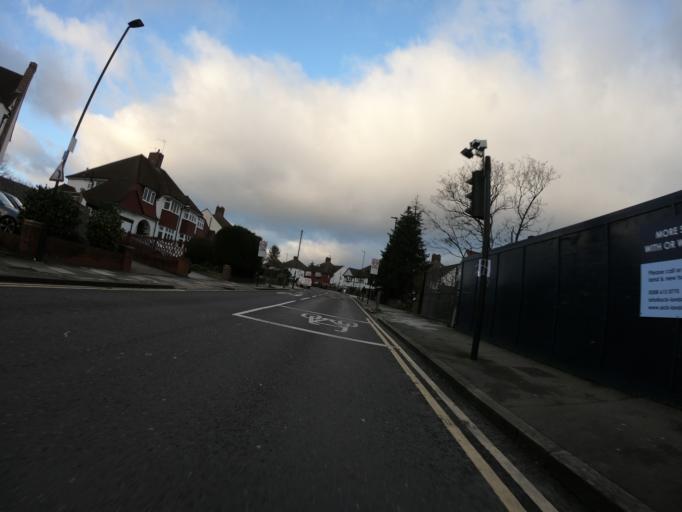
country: GB
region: England
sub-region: Greater London
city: Welling
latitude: 51.4513
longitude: 0.0788
